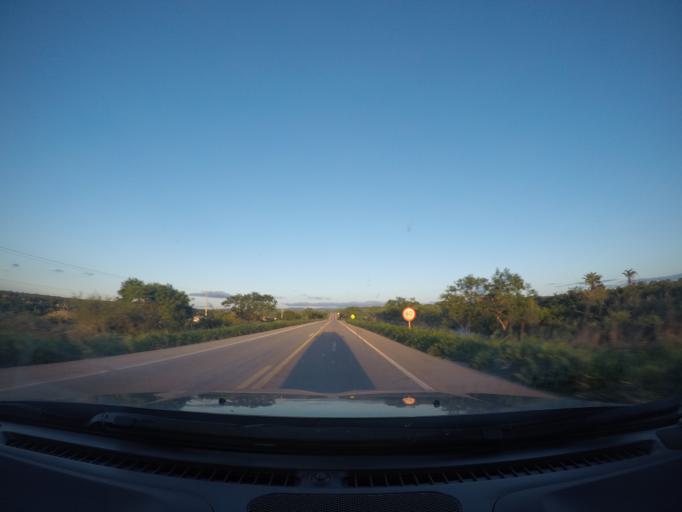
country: BR
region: Bahia
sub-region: Seabra
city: Seabra
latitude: -12.3972
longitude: -41.9353
